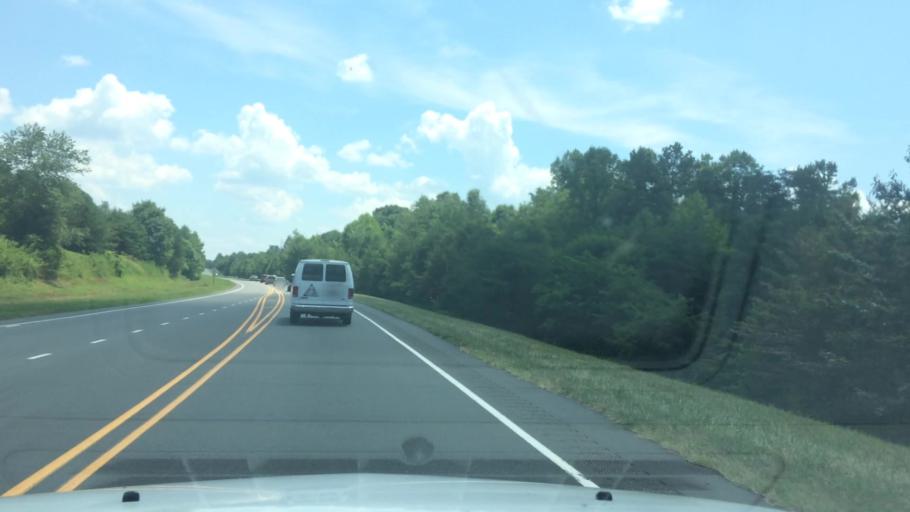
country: US
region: North Carolina
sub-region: Alexander County
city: Stony Point
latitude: 35.8246
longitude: -81.0120
